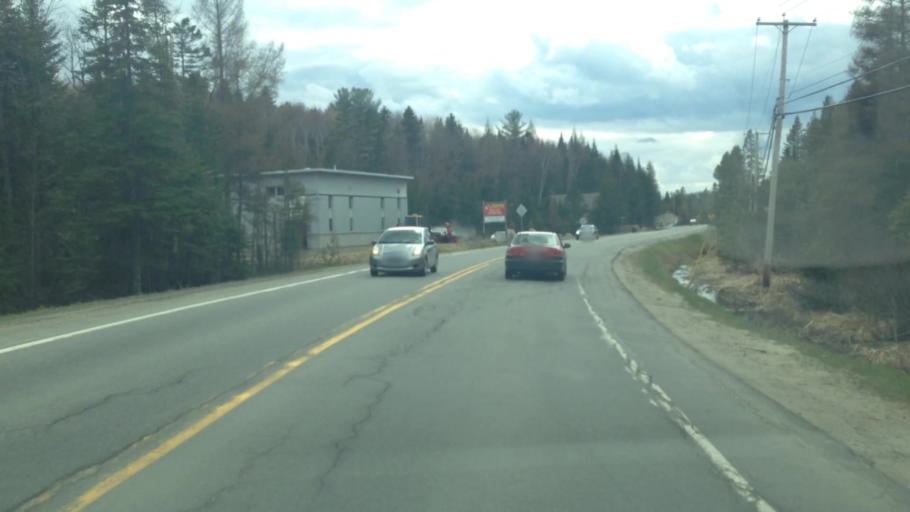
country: CA
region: Quebec
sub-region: Laurentides
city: Sainte-Adele
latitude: 46.0199
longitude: -74.0767
